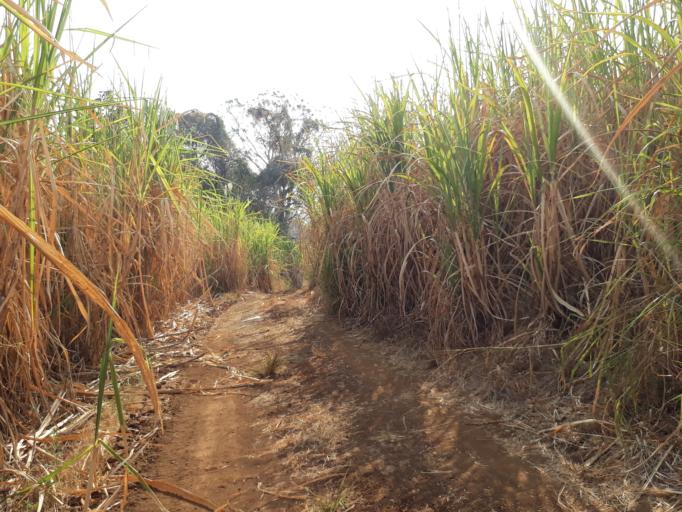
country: CR
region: Alajuela
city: Atenas
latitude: 10.0239
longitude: -84.3386
